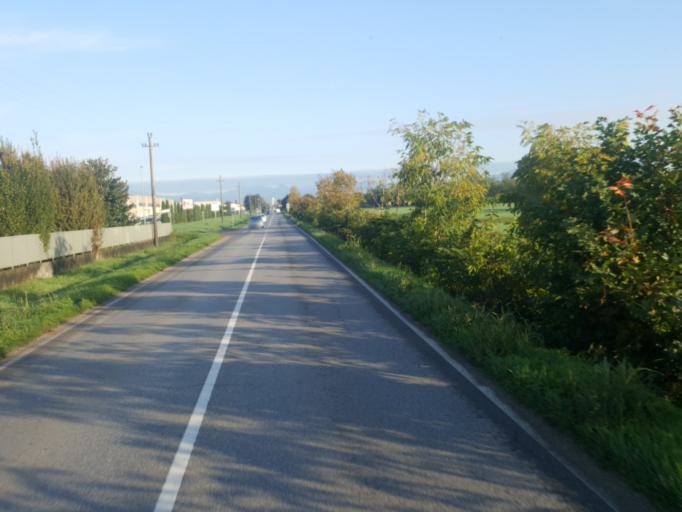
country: IT
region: Lombardy
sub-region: Provincia di Bergamo
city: Cologno al Serio
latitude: 45.5609
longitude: 9.7076
